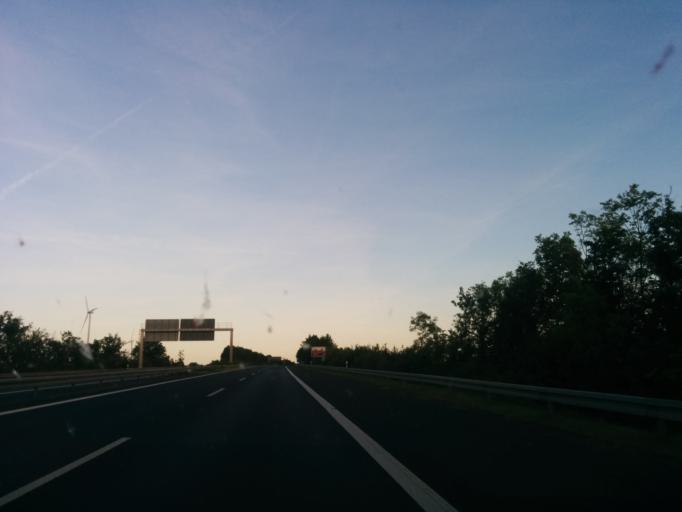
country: DE
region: Bavaria
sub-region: Regierungsbezirk Unterfranken
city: Biebelried
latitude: 49.7736
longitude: 10.0964
